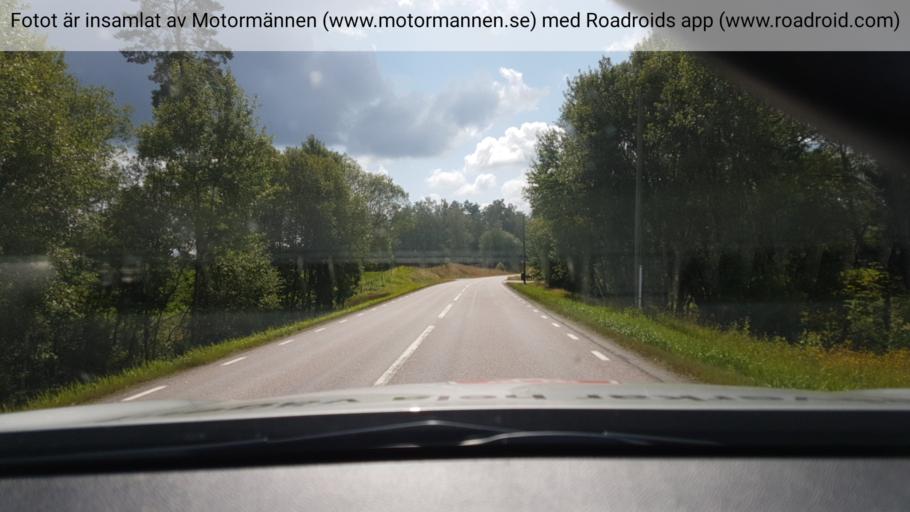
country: SE
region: Vaestra Goetaland
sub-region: Svenljunga Kommun
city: Svenljunga
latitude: 57.4868
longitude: 13.0591
